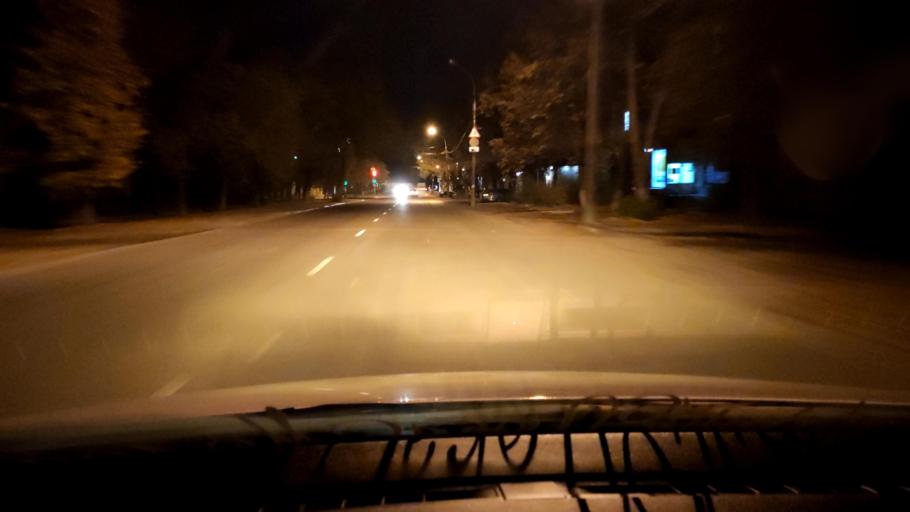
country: RU
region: Voronezj
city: Voronezh
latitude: 51.6771
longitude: 39.1579
